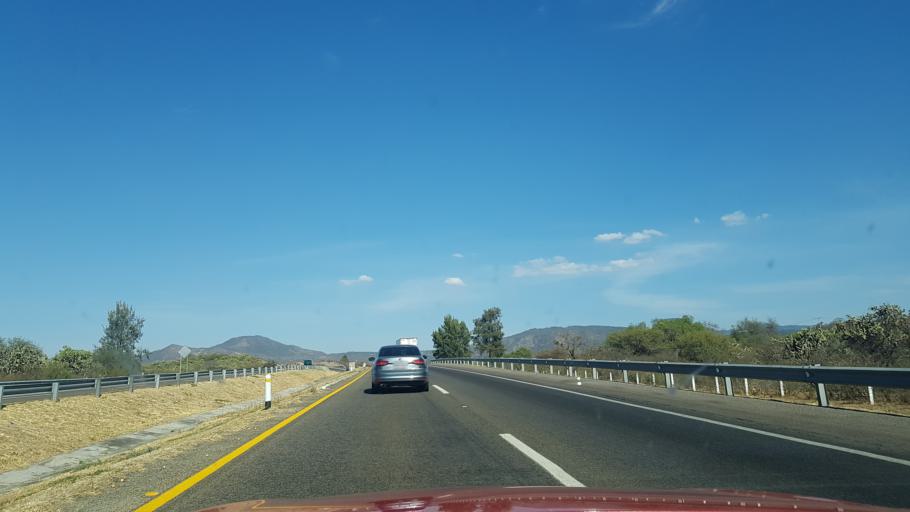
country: MX
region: Michoacan
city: Zinapecuaro
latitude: 19.9009
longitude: -100.8214
